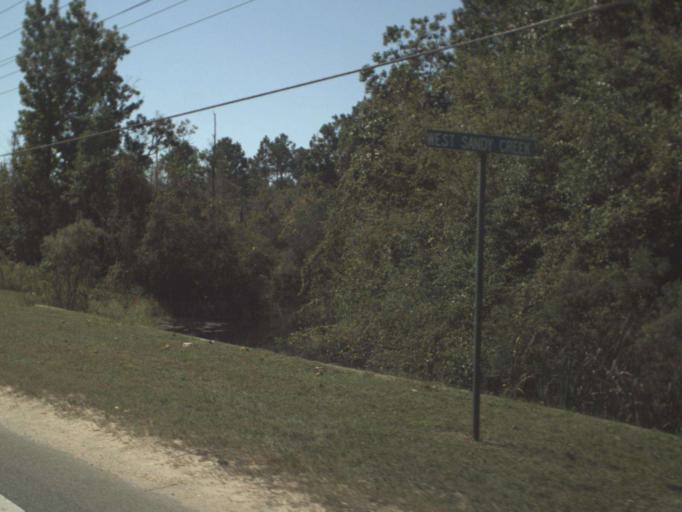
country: US
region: Florida
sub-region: Walton County
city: DeFuniak Springs
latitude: 30.7370
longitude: -86.1152
